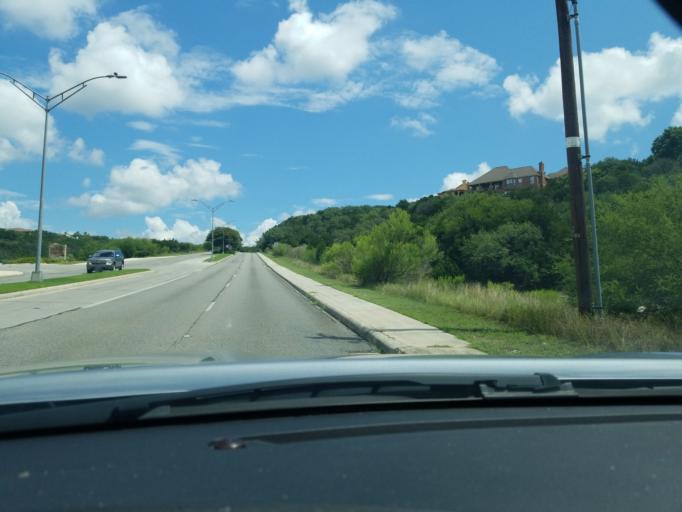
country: US
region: Texas
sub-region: Bexar County
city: Hollywood Park
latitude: 29.6471
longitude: -98.4811
